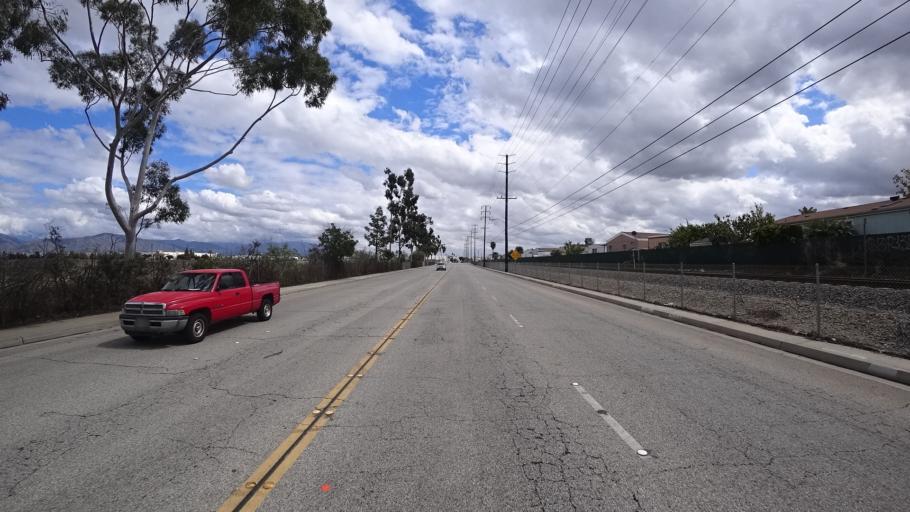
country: US
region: California
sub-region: Los Angeles County
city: Baldwin Park
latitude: 34.0926
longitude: -117.9477
